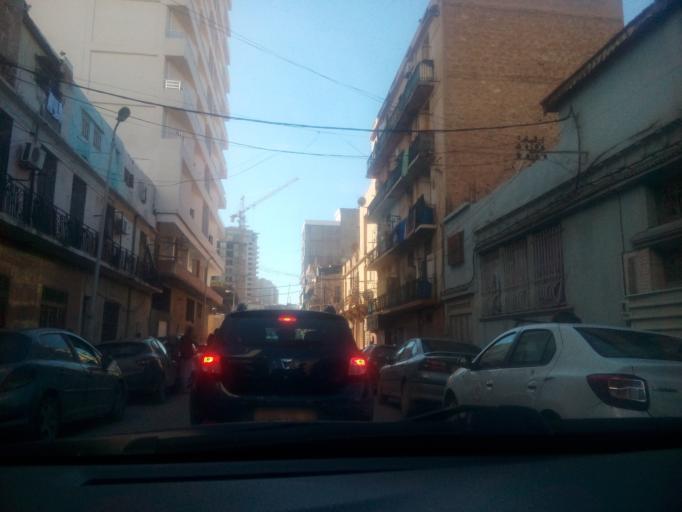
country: DZ
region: Oran
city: Oran
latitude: 35.7086
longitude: -0.6210
